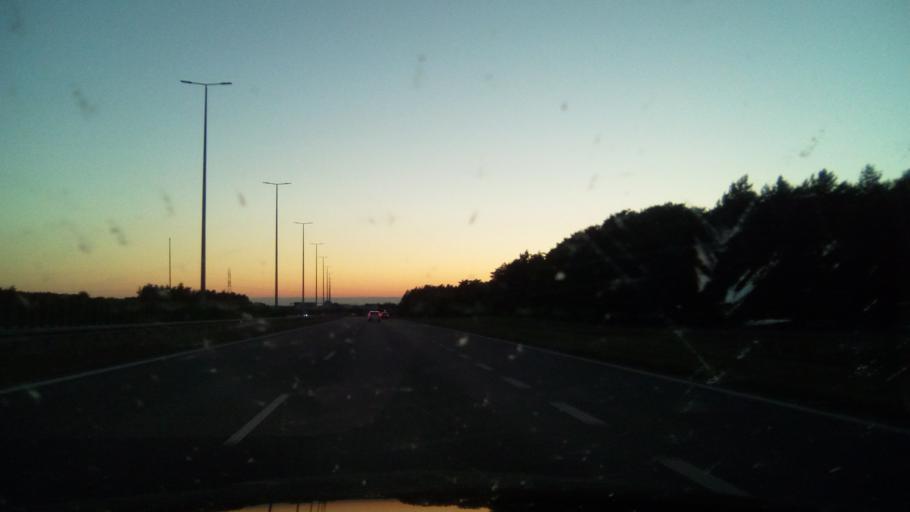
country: PL
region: Greater Poland Voivodeship
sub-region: Powiat koninski
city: Stare Miasto
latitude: 52.1569
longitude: 18.2639
